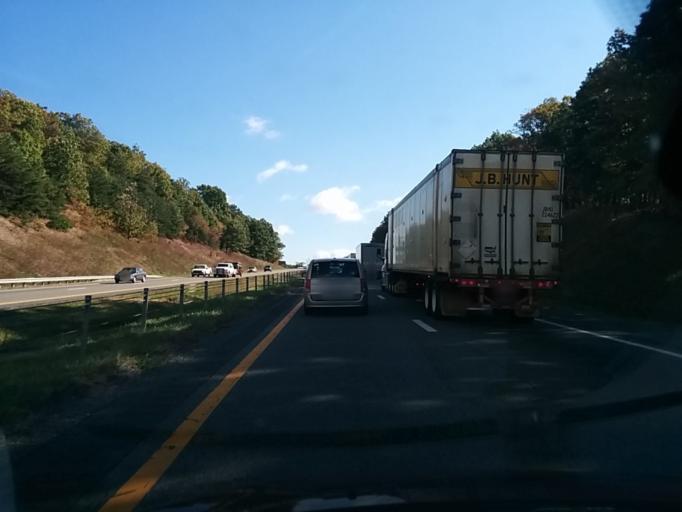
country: US
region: Virginia
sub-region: City of Waynesboro
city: Waynesboro
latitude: 38.0400
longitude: -78.8829
